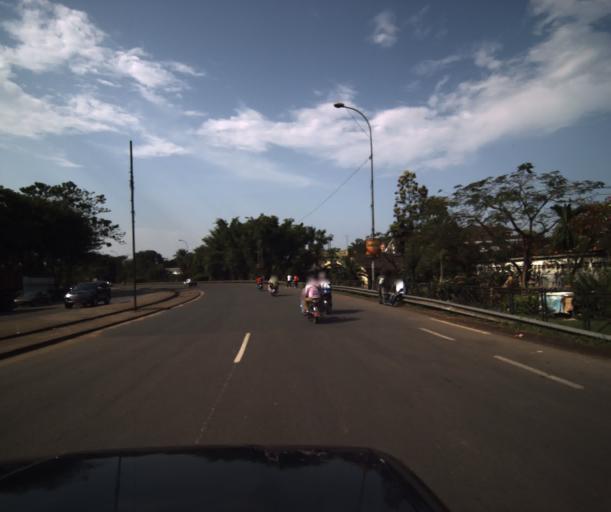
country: CM
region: Littoral
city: Douala
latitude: 4.0256
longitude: 9.6925
